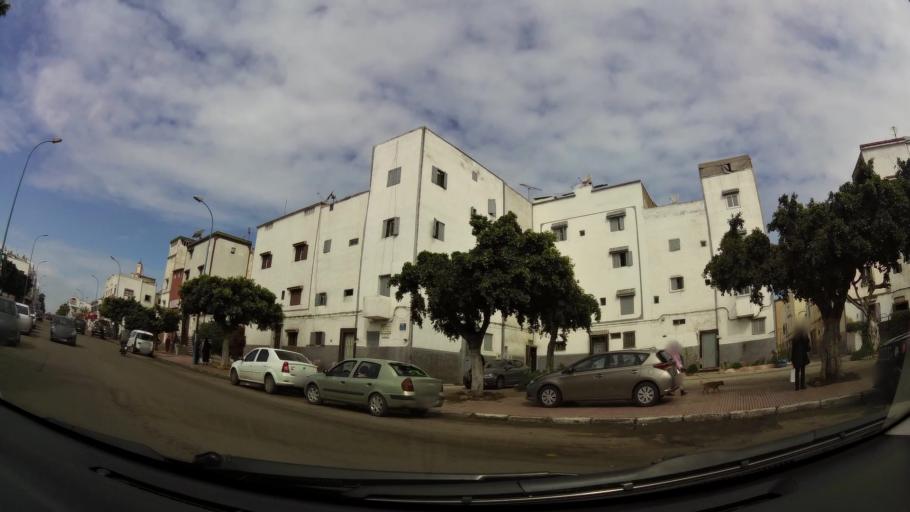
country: MA
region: Grand Casablanca
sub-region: Casablanca
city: Casablanca
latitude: 33.5734
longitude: -7.6716
